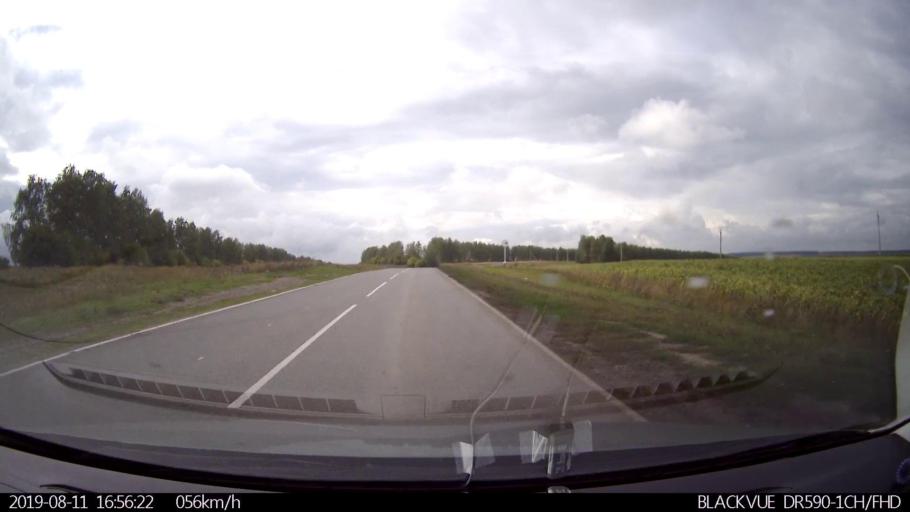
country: RU
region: Ulyanovsk
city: Mayna
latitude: 54.2871
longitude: 47.6544
